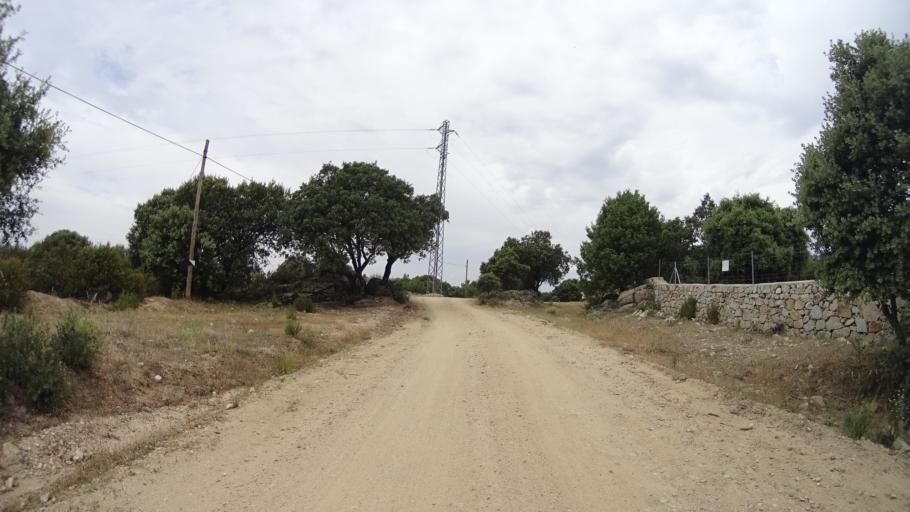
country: ES
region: Madrid
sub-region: Provincia de Madrid
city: Colmenarejo
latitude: 40.5468
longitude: -4.0384
